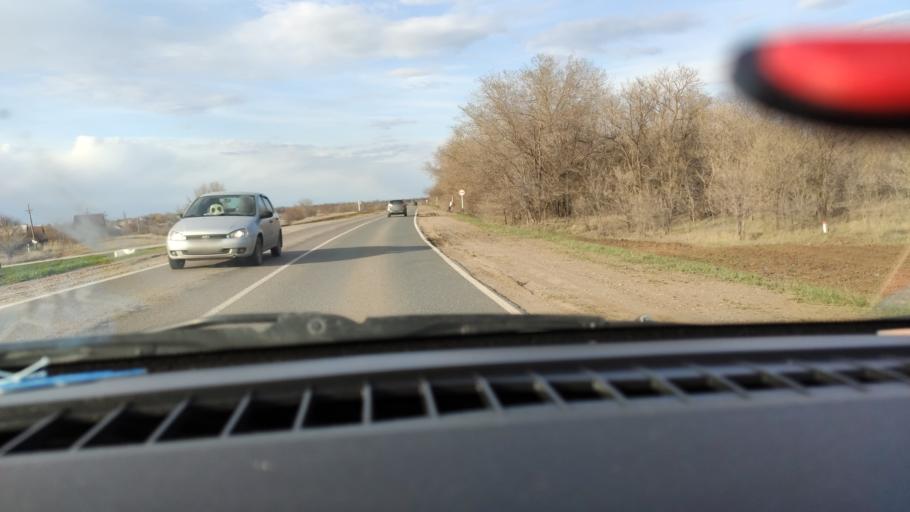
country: RU
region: Saratov
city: Privolzhskiy
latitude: 51.3467
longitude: 46.0443
